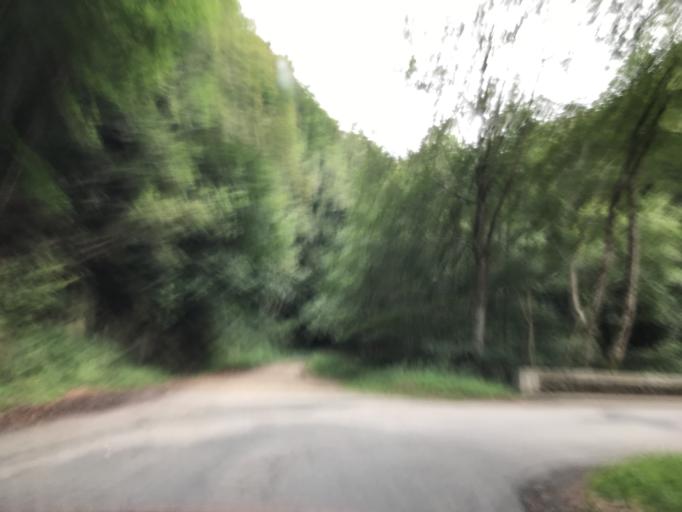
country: FR
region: Rhone-Alpes
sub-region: Departement de la Loire
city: Sail-sous-Couzan
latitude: 45.6837
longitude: 3.9012
